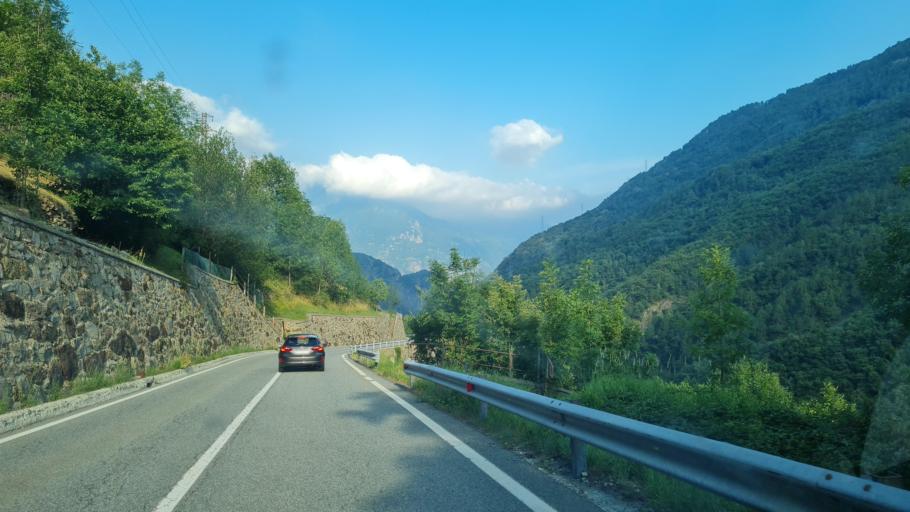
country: IT
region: Aosta Valley
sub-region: Valle d'Aosta
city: Hone
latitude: 45.6115
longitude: 7.7177
